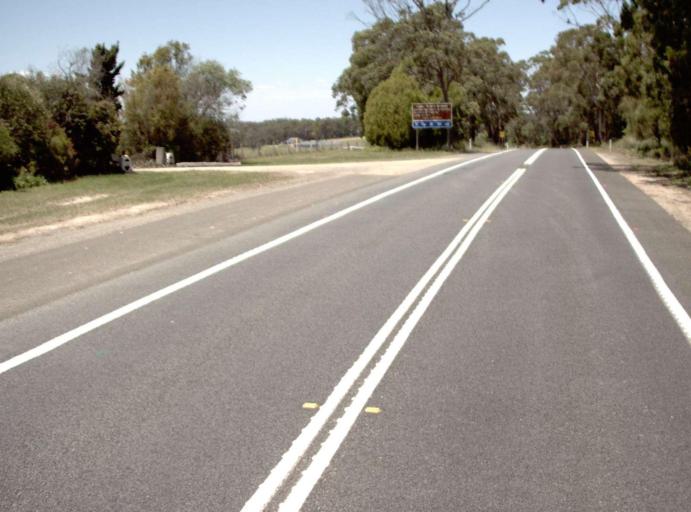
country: AU
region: Victoria
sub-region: East Gippsland
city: Lakes Entrance
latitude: -37.8418
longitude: 148.0369
